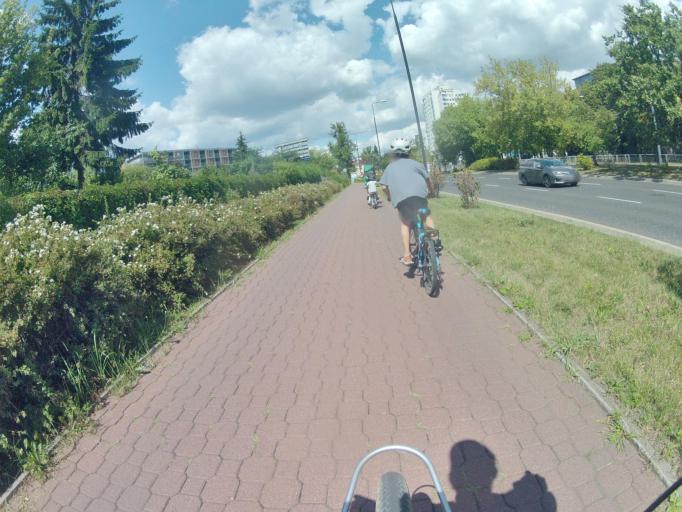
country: PL
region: Masovian Voivodeship
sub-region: Warszawa
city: Ochota
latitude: 52.2043
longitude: 20.9993
